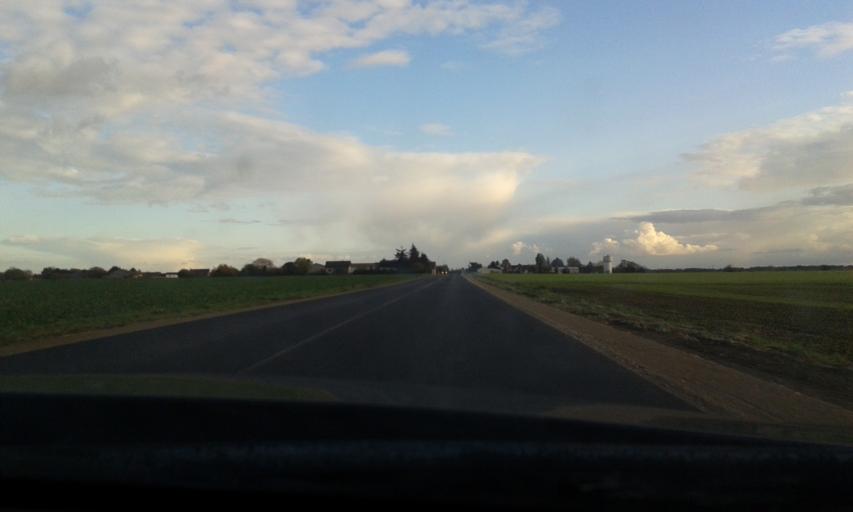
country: FR
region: Centre
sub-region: Departement d'Eure-et-Loir
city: Le Coudray
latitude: 48.4204
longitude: 1.5268
